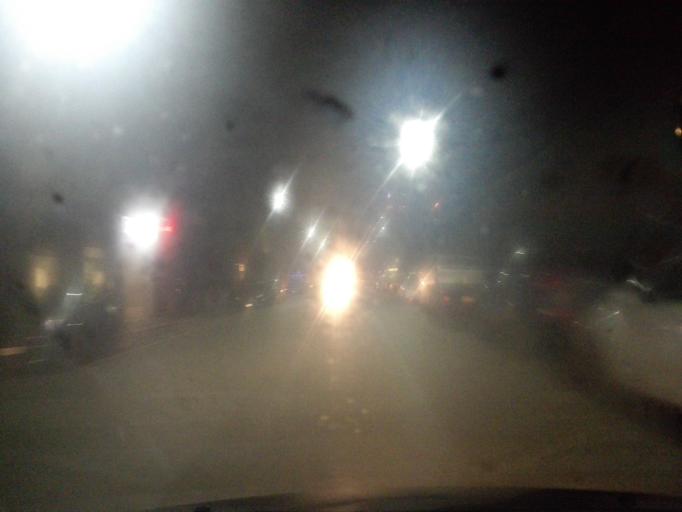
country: IT
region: Piedmont
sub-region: Provincia di Alessandria
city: Alessandria
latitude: 44.9095
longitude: 8.6214
